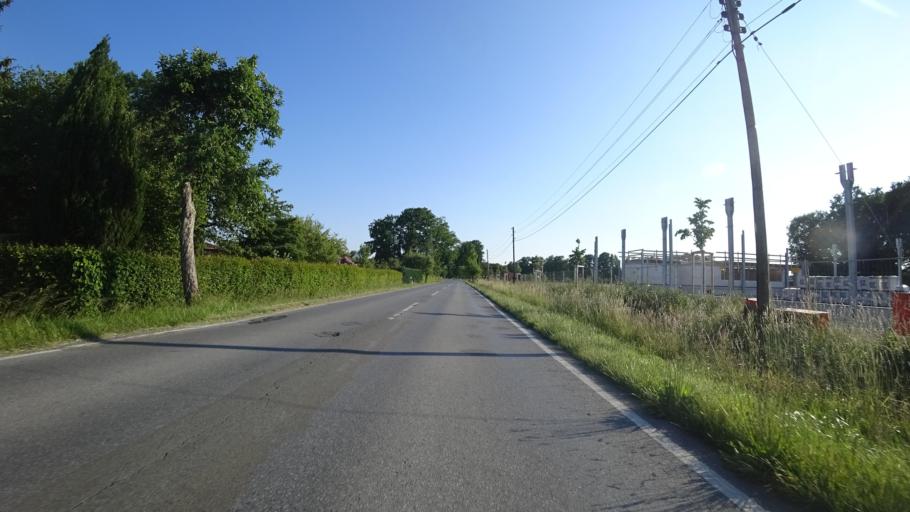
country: DE
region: North Rhine-Westphalia
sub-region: Regierungsbezirk Detmold
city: Steinhagen
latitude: 51.9619
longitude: 8.4170
